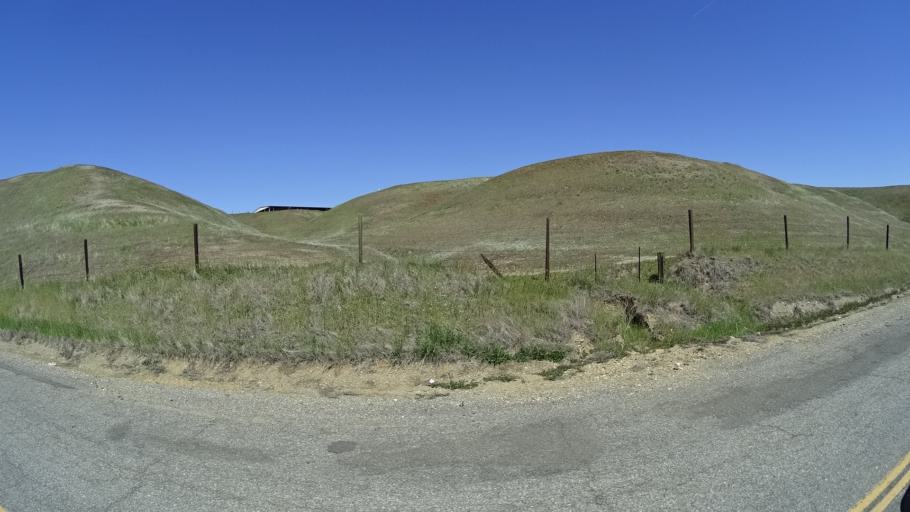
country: US
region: California
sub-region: Glenn County
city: Orland
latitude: 39.7804
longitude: -122.3055
